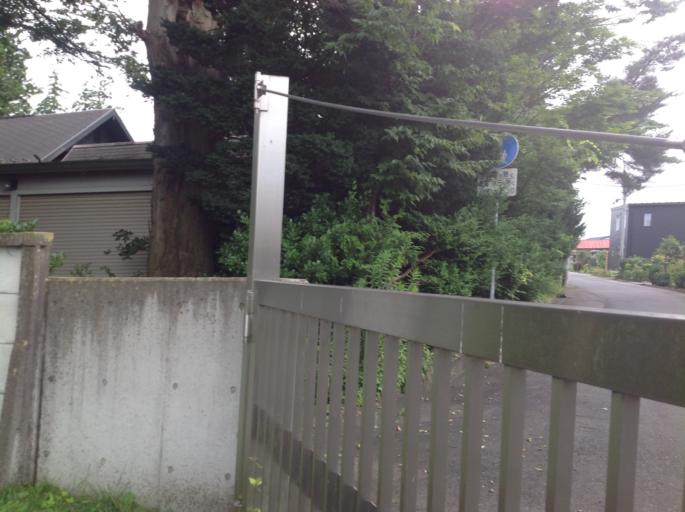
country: JP
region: Iwate
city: Mizusawa
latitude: 39.1341
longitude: 141.1313
